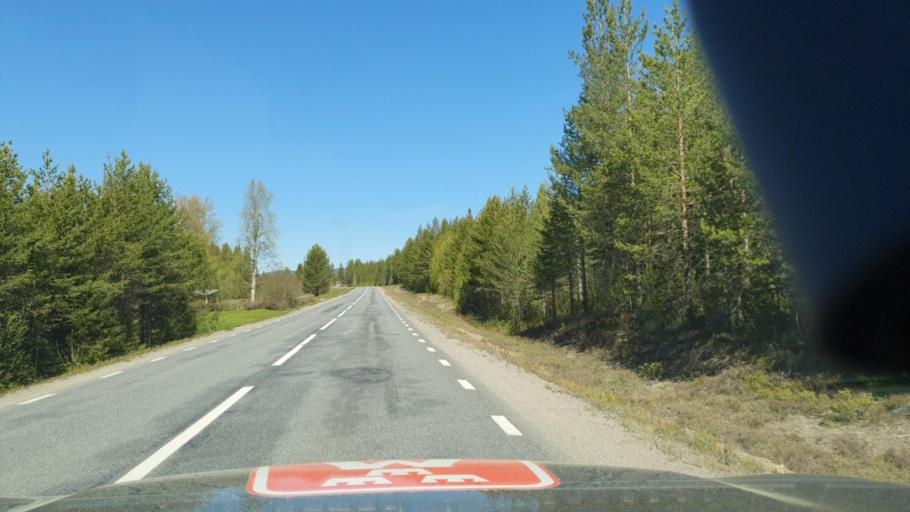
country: SE
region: Vaesternorrland
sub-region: OErnskoeldsviks Kommun
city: Bredbyn
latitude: 63.7395
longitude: 18.5005
